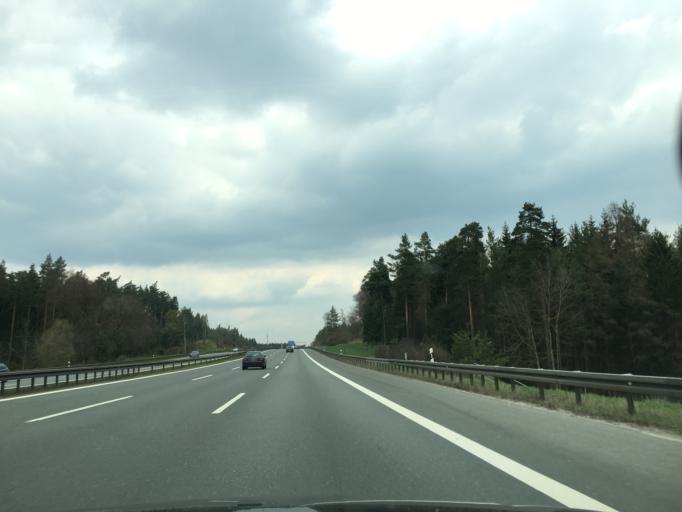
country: DE
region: Bavaria
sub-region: Regierungsbezirk Mittelfranken
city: Velden
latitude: 49.6890
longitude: 11.4664
